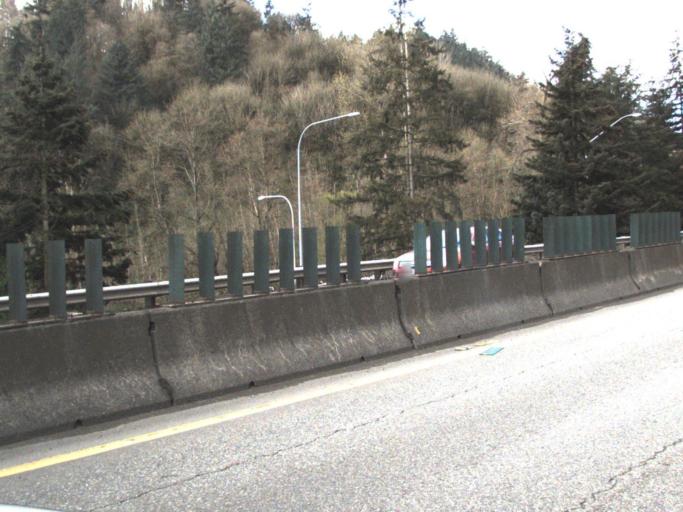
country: US
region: Washington
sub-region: King County
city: Algona
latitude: 47.3032
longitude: -122.2576
